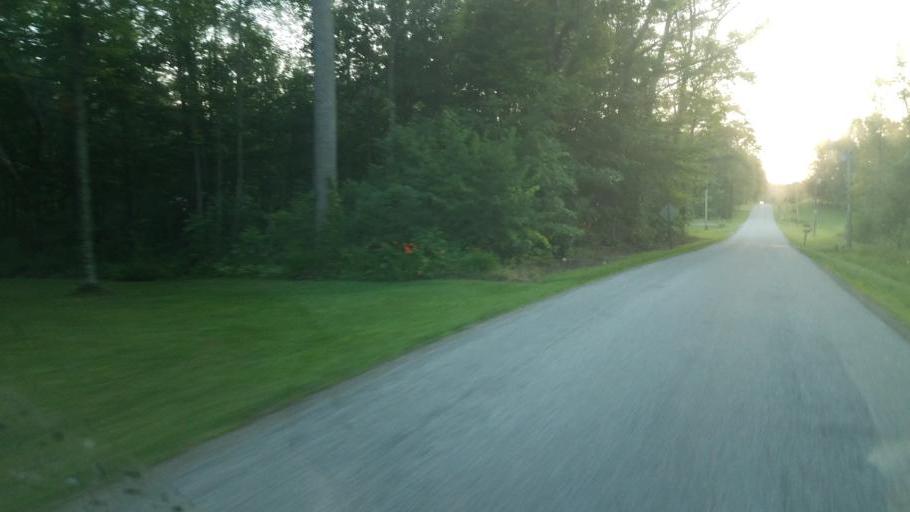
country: US
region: Ohio
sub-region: Morrow County
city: Mount Gilead
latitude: 40.5221
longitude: -82.7434
